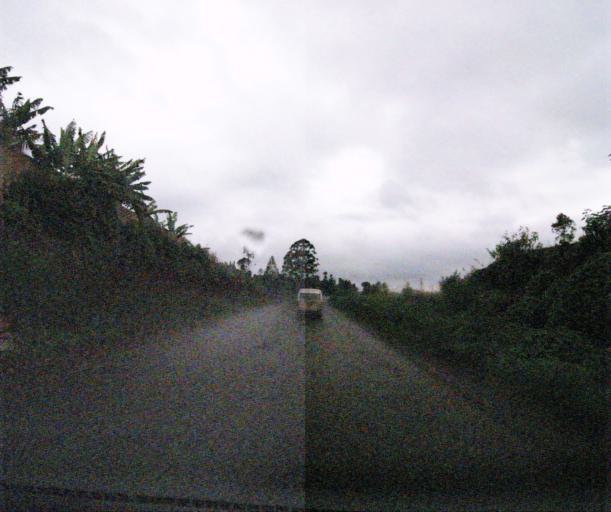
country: CM
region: West
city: Bansoa
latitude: 5.4985
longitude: 10.2512
